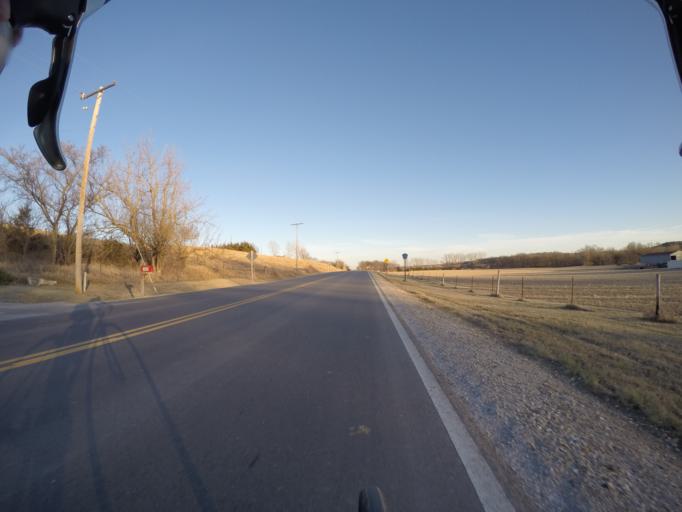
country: US
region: Kansas
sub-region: Riley County
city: Ogden
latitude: 39.2229
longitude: -96.7052
